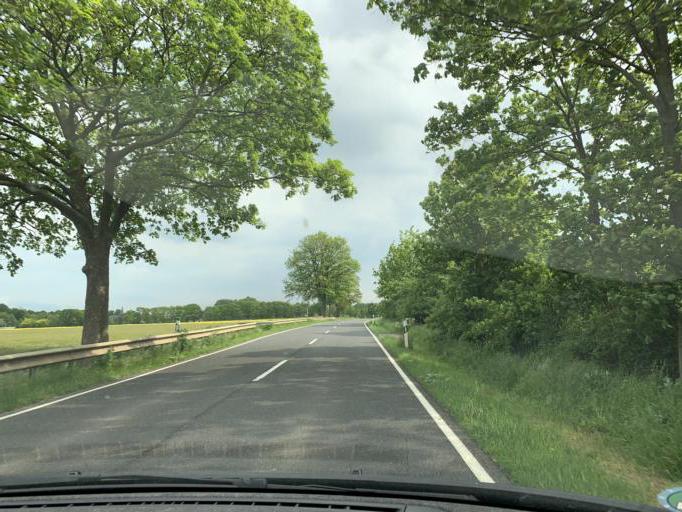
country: DE
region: North Rhine-Westphalia
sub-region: Regierungsbezirk Koln
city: Norvenich
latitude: 50.7691
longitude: 6.6334
